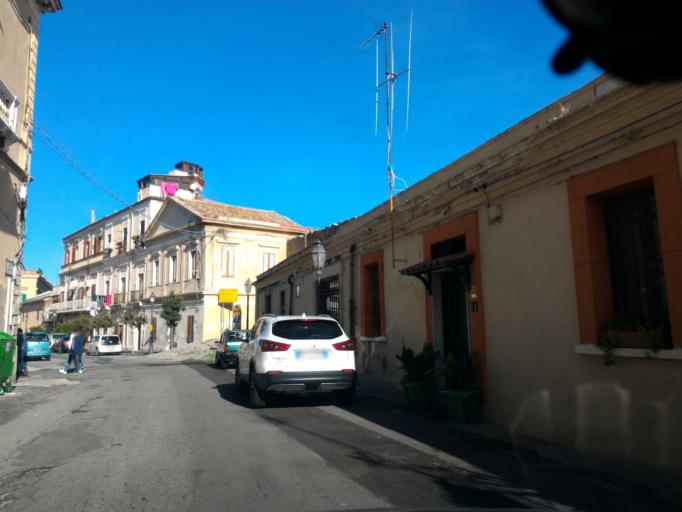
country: IT
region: Calabria
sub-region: Provincia di Crotone
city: Crotone
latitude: 39.0812
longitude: 17.1312
